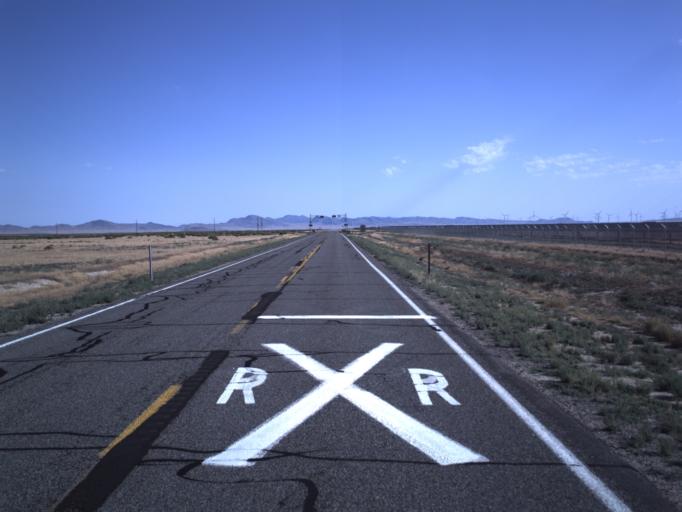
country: US
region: Utah
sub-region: Beaver County
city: Milford
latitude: 38.4912
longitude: -112.9911
